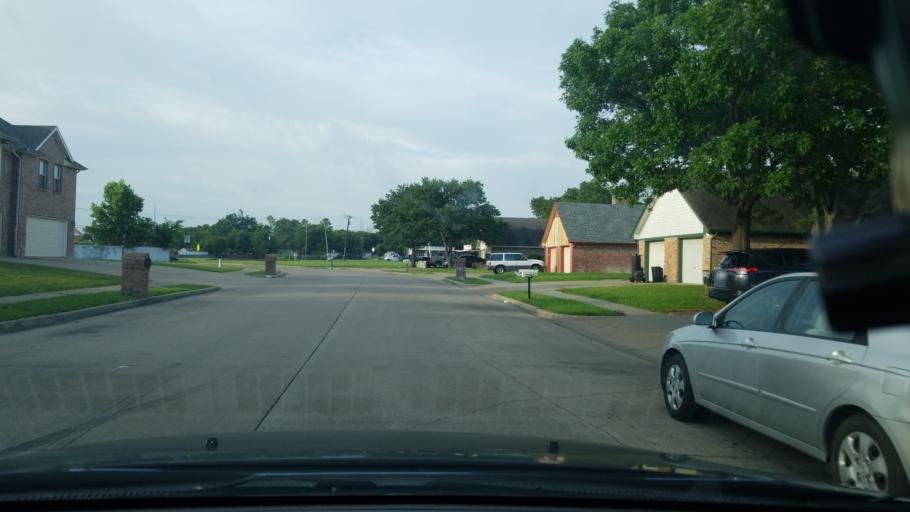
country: US
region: Texas
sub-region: Dallas County
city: Mesquite
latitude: 32.8232
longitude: -96.6494
